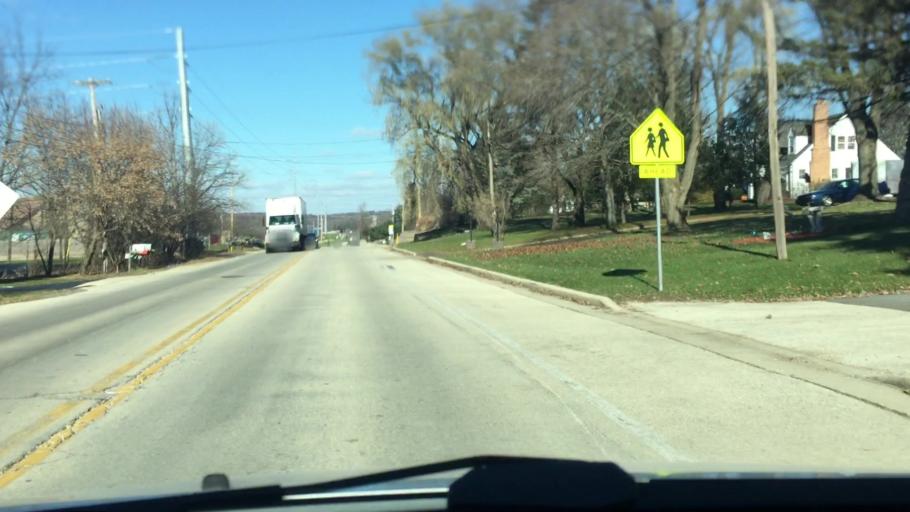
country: US
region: Wisconsin
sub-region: Waukesha County
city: Pewaukee
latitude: 43.0560
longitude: -88.3041
